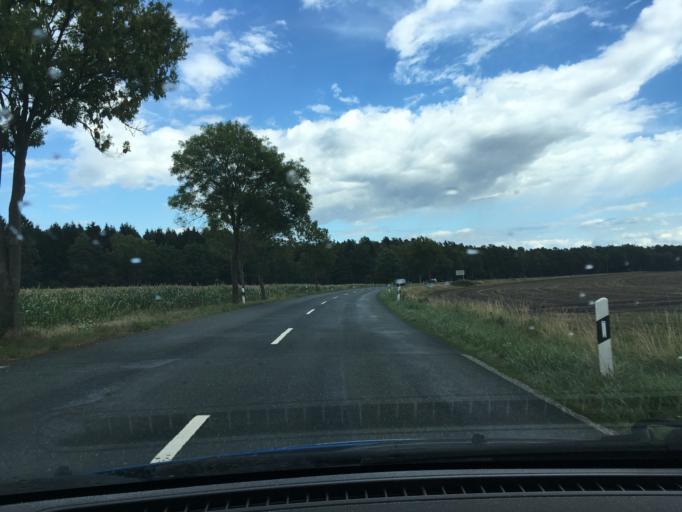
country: DE
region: Lower Saxony
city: Wietzendorf
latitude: 52.9351
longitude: 9.9935
